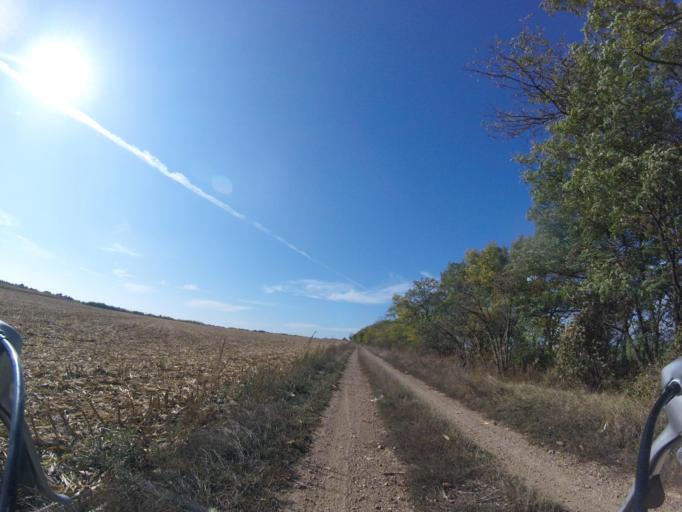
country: HU
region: Fejer
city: Zamoly
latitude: 47.2813
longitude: 18.4451
